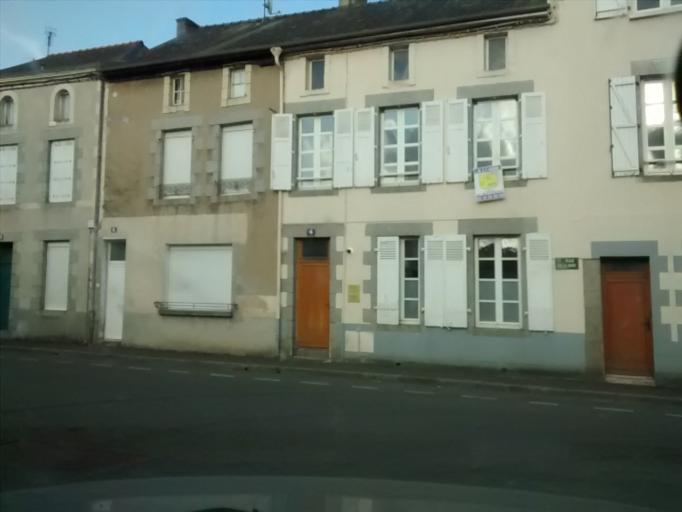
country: FR
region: Pays de la Loire
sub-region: Departement de la Mayenne
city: Montsurs
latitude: 48.1372
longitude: -0.5538
